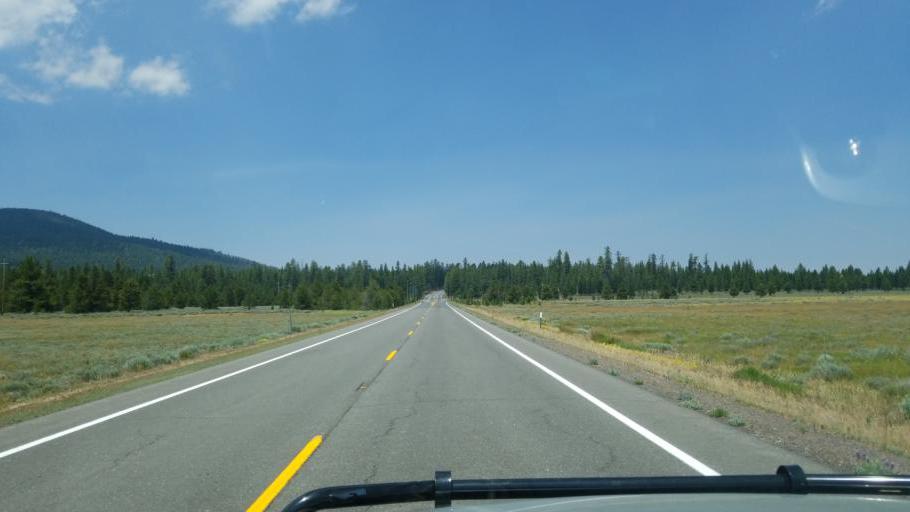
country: US
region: California
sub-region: Lassen County
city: Westwood
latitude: 40.5817
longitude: -121.0839
